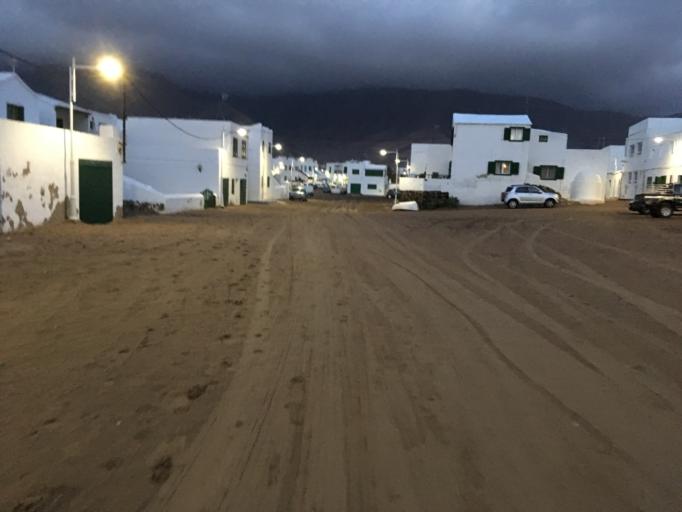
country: ES
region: Canary Islands
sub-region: Provincia de Las Palmas
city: Teguise
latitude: 29.1186
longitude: -13.5658
